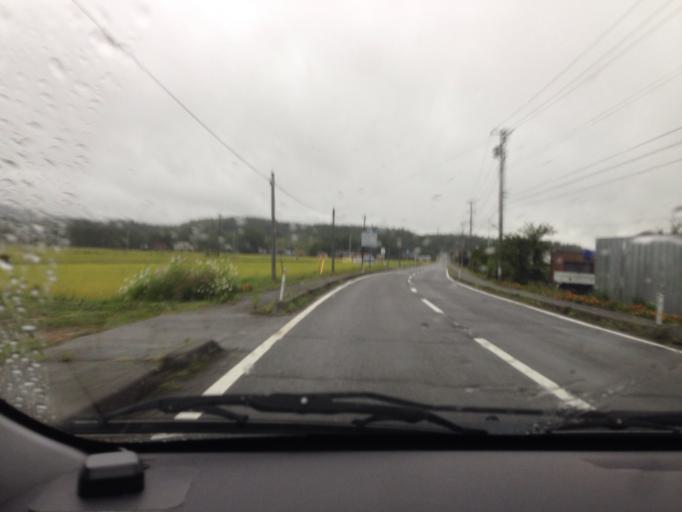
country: JP
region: Fukushima
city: Koriyama
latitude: 37.3997
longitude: 140.2683
